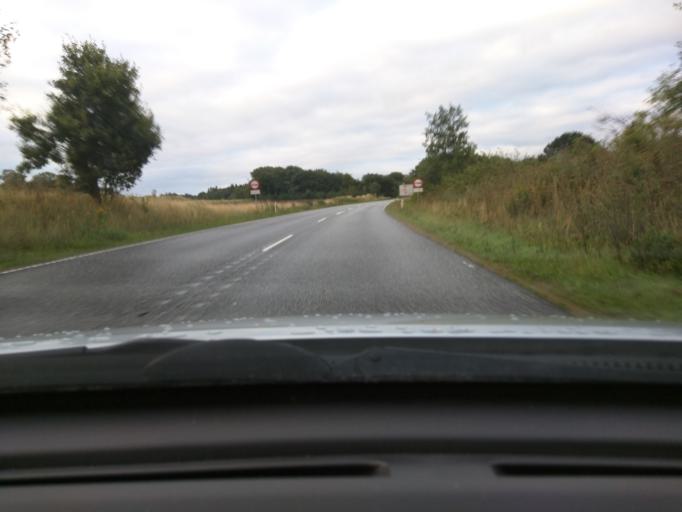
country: DK
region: Central Jutland
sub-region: Viborg Kommune
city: Viborg
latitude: 56.3606
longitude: 9.3674
